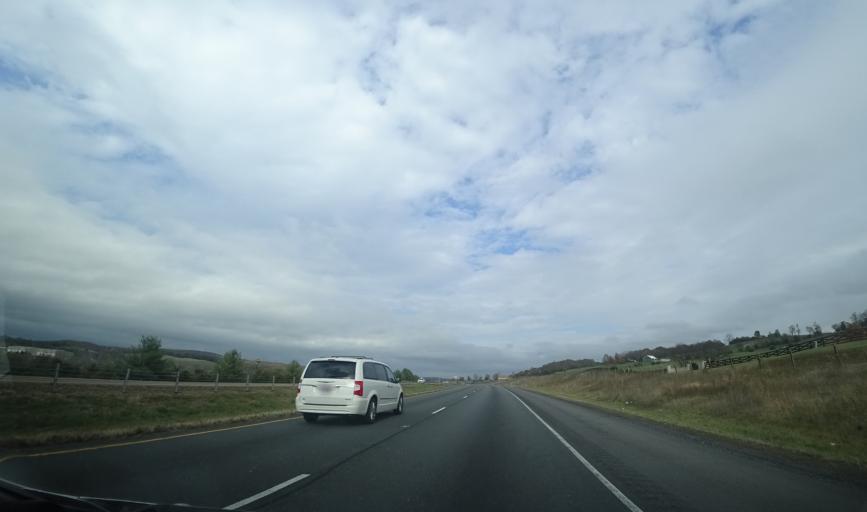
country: US
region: Virginia
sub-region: City of Harrisonburg
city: Harrisonburg
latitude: 38.4737
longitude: -78.8138
